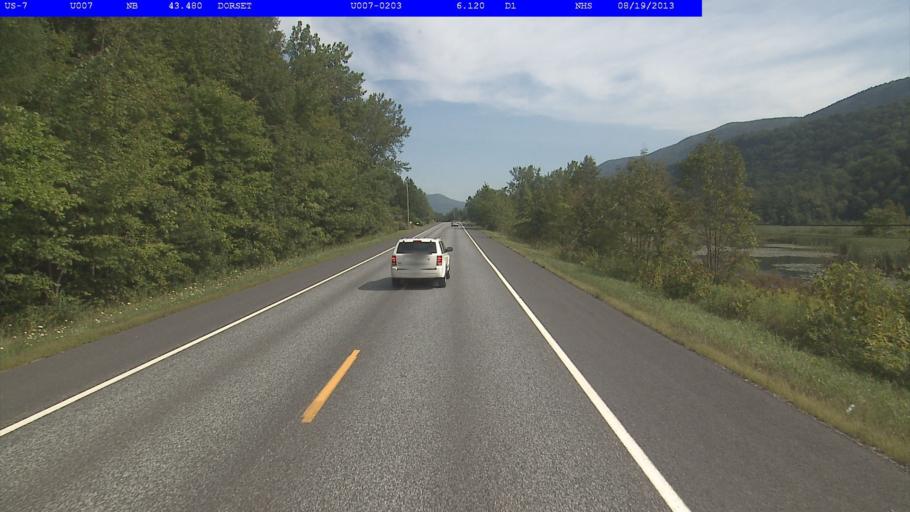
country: US
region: Vermont
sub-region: Bennington County
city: Manchester Center
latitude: 43.2965
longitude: -72.9974
